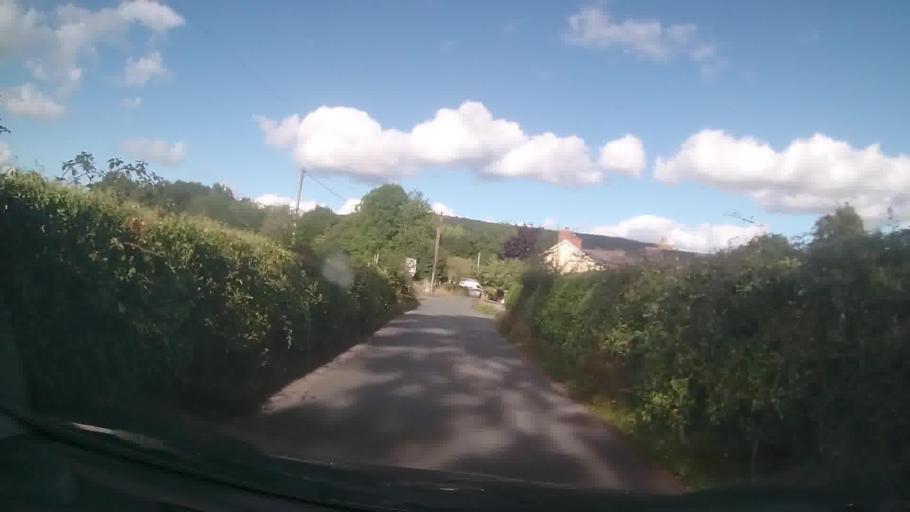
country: GB
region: Wales
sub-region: Sir Powys
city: Brecon
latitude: 51.8951
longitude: -3.2922
